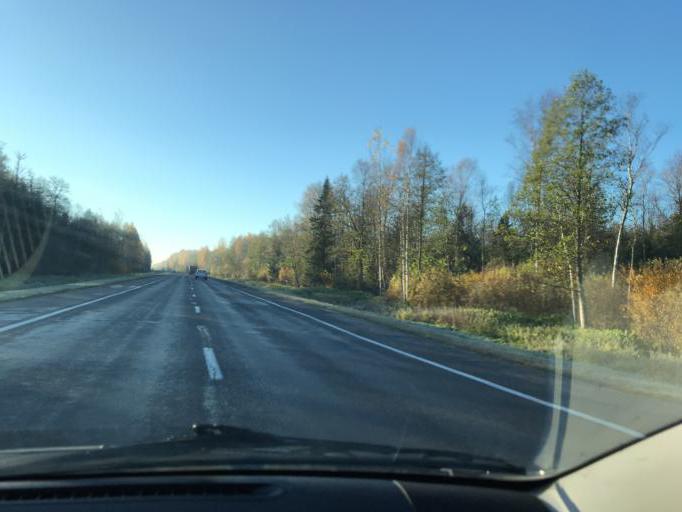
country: BY
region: Vitebsk
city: Vitebsk
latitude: 54.9586
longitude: 30.3568
